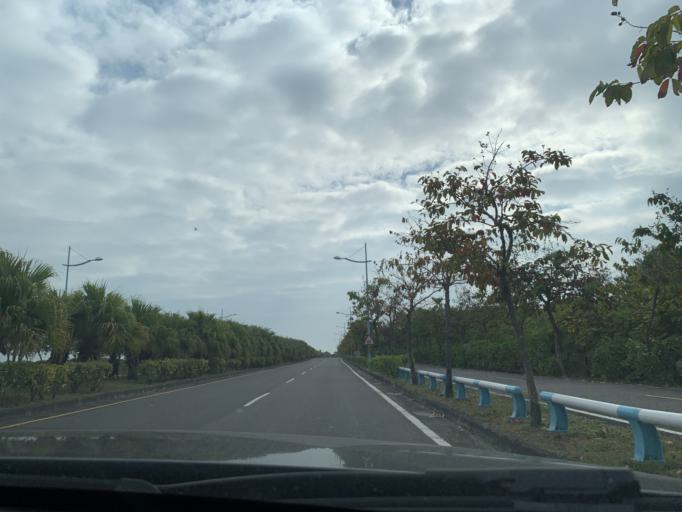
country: TW
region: Taiwan
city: Fengshan
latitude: 22.4511
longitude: 120.4878
